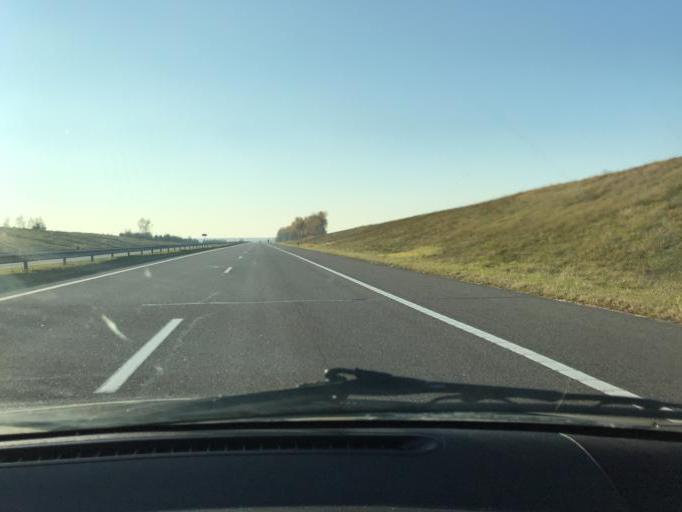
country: BY
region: Minsk
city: Loshnitsa
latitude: 54.2907
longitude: 28.7919
